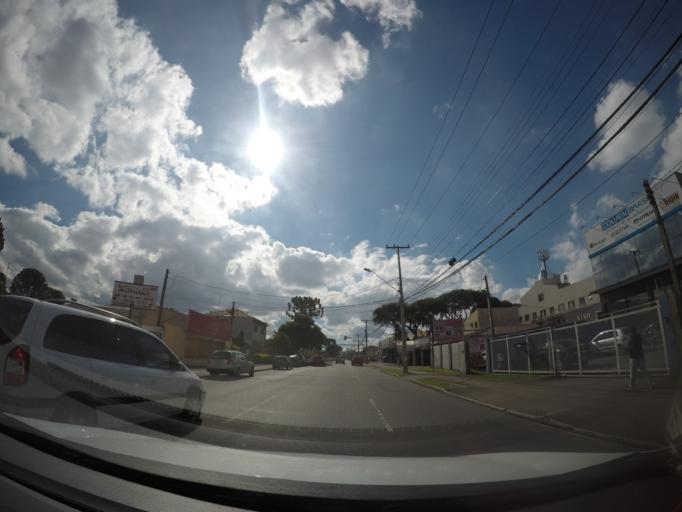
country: BR
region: Parana
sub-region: Curitiba
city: Curitiba
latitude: -25.4795
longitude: -49.2551
